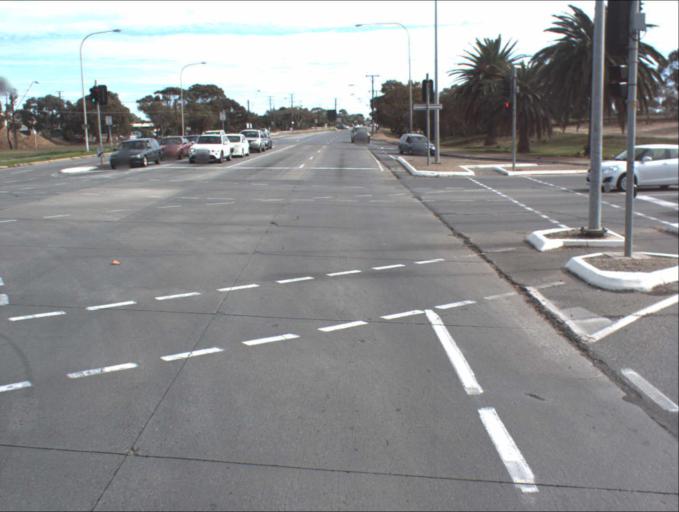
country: AU
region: South Australia
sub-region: Charles Sturt
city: West Lakes Shore
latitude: -34.8524
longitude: 138.5024
